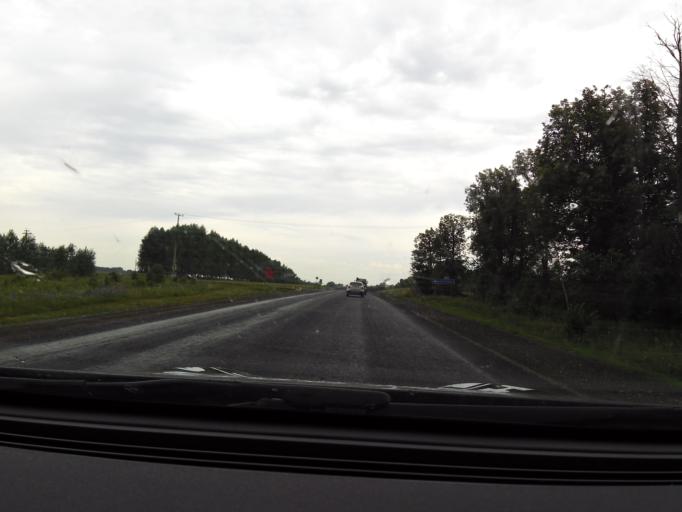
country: RU
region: Bashkortostan
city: Iglino
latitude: 54.7865
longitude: 56.5387
